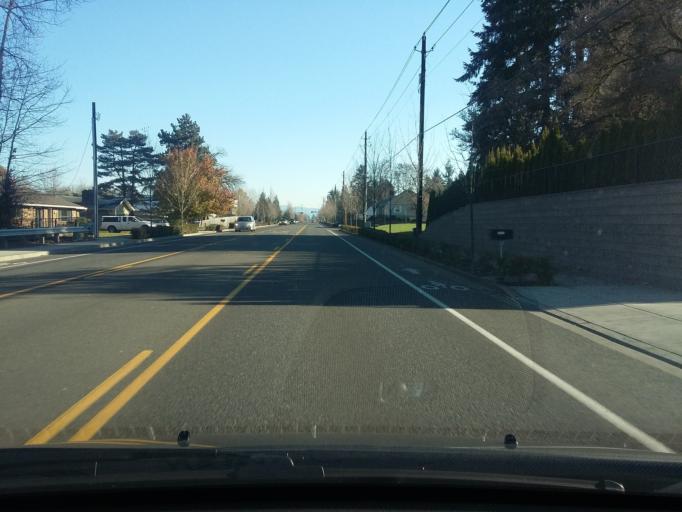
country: US
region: Washington
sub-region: Clark County
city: Barberton
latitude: 45.6860
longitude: -122.6205
